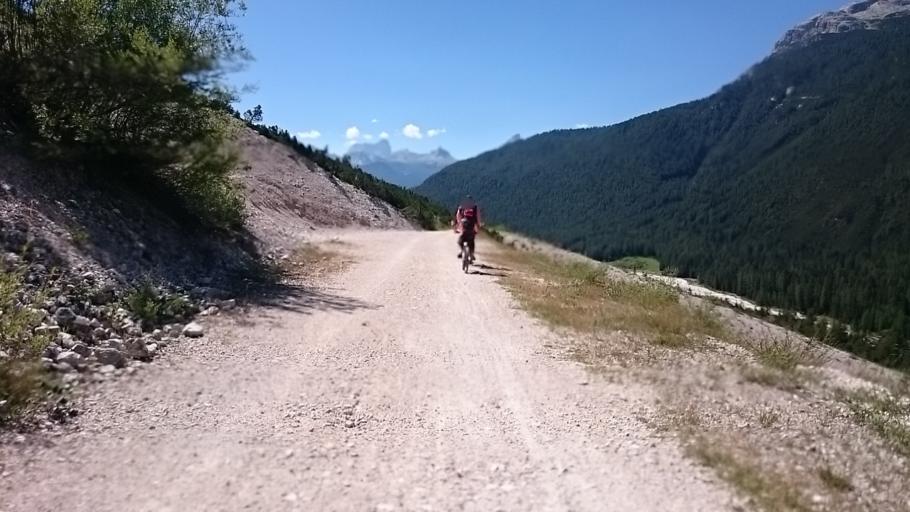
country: IT
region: Veneto
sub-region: Provincia di Belluno
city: Cortina d'Ampezzo
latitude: 46.5863
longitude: 12.1156
